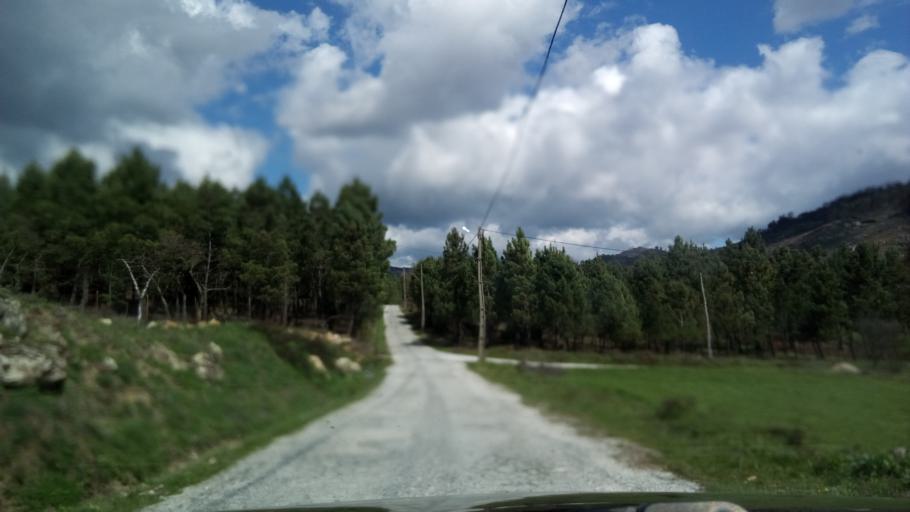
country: PT
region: Guarda
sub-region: Fornos de Algodres
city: Fornos de Algodres
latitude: 40.6479
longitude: -7.5040
